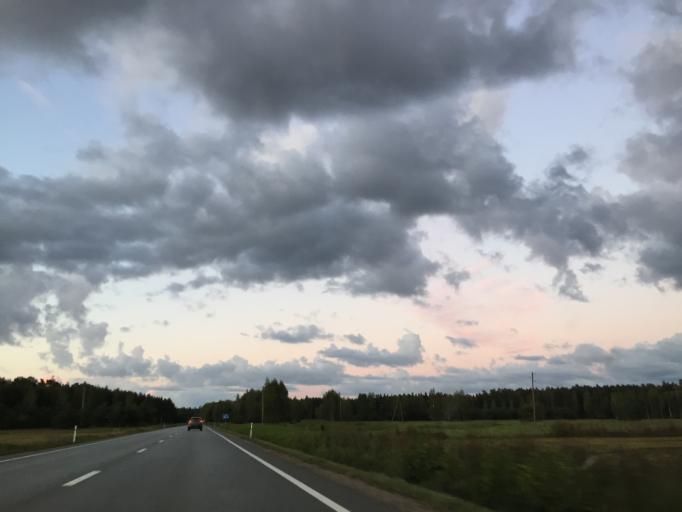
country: LV
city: Tireli
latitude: 56.8580
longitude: 23.6102
